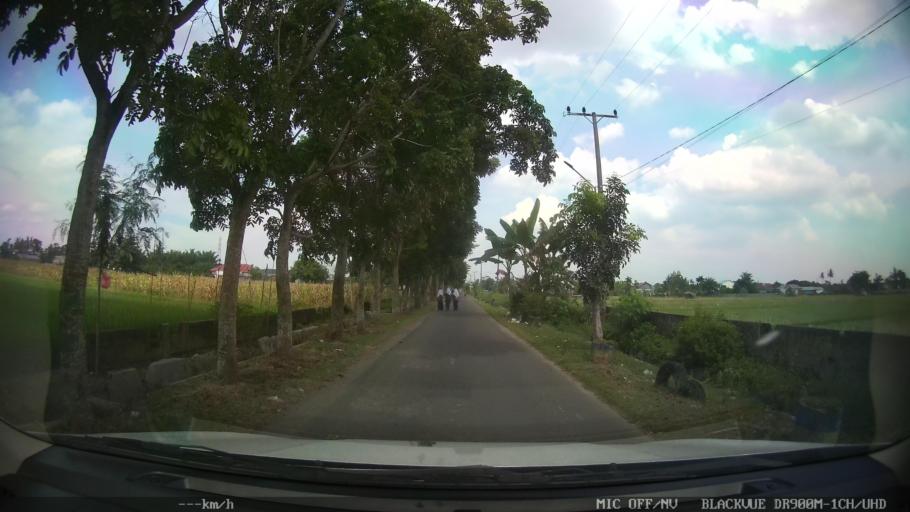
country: ID
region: North Sumatra
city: Binjai
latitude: 3.6209
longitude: 98.5143
